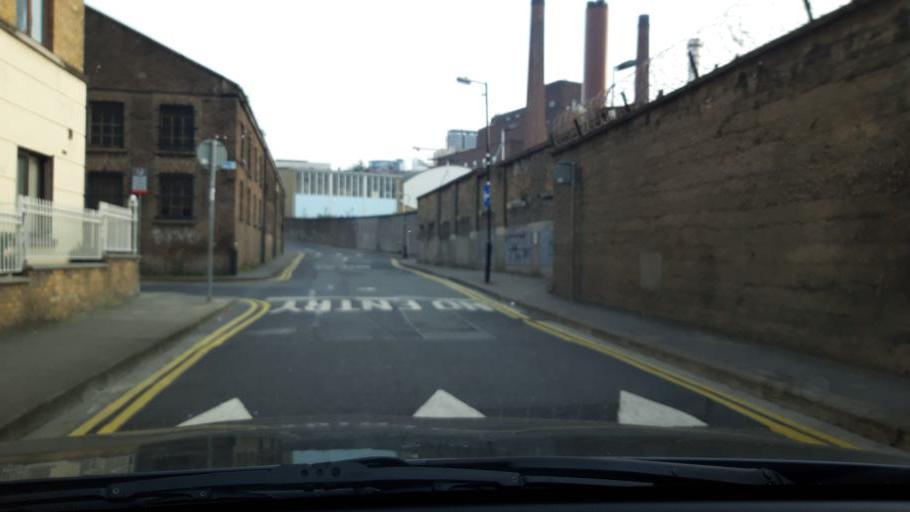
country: IE
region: Leinster
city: Rialto
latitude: 53.3456
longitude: -6.2846
